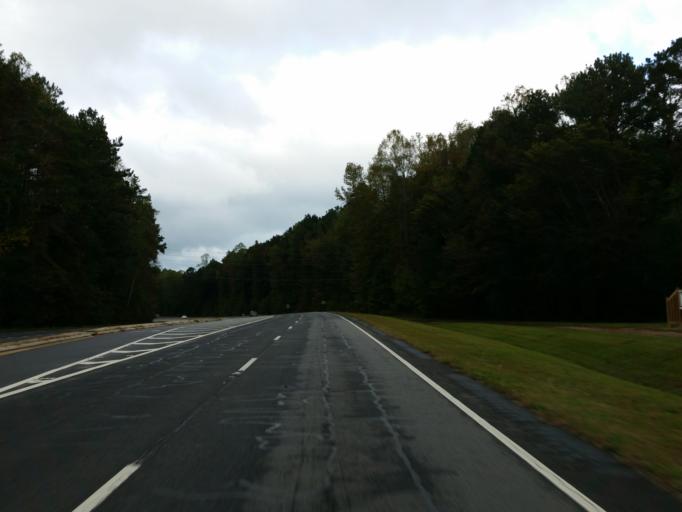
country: US
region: Georgia
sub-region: Bartow County
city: Emerson
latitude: 34.0946
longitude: -84.7402
